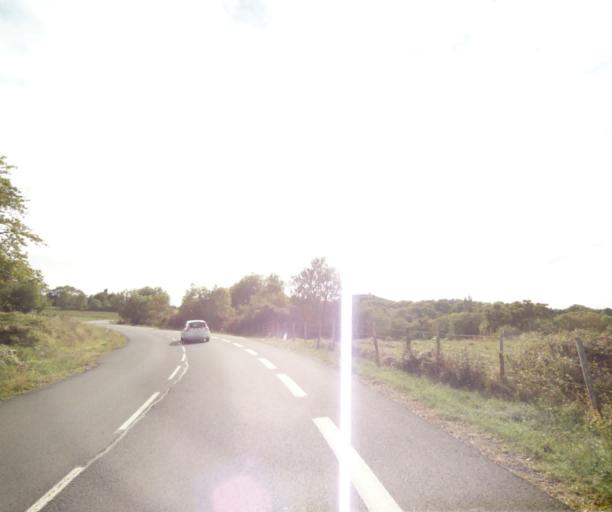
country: FR
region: Auvergne
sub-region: Departement du Puy-de-Dome
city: Romagnat
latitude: 45.7181
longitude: 3.0912
